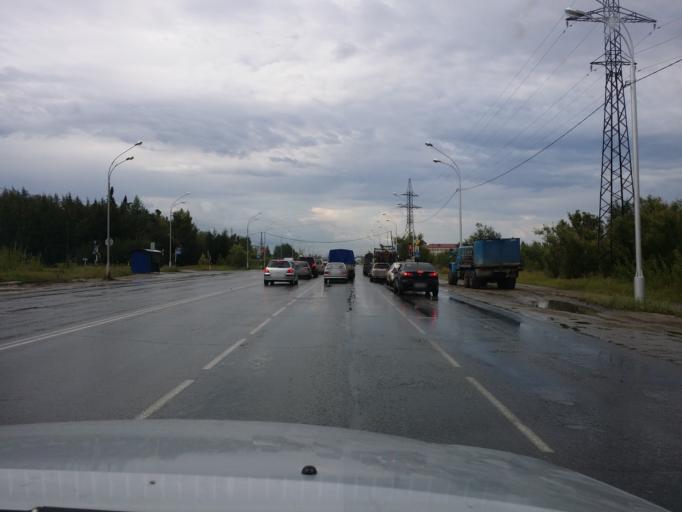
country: RU
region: Khanty-Mansiyskiy Avtonomnyy Okrug
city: Nizhnevartovsk
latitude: 60.9544
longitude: 76.5302
